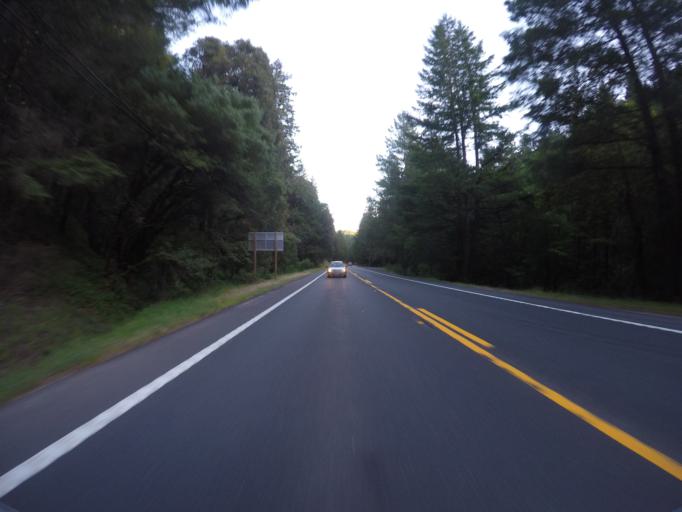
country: US
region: California
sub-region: Mendocino County
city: Laytonville
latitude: 39.8026
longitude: -123.5435
